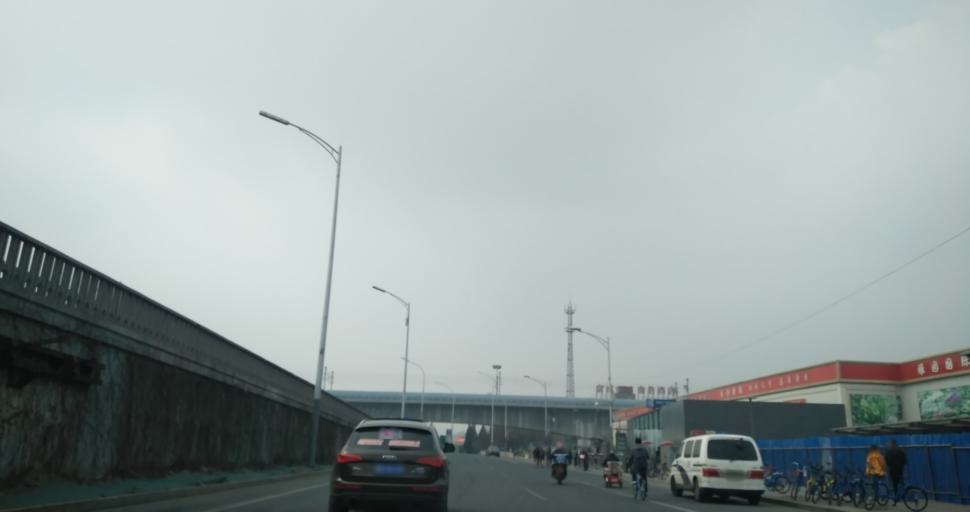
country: CN
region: Beijing
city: Longtan
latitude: 39.8644
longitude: 116.4518
